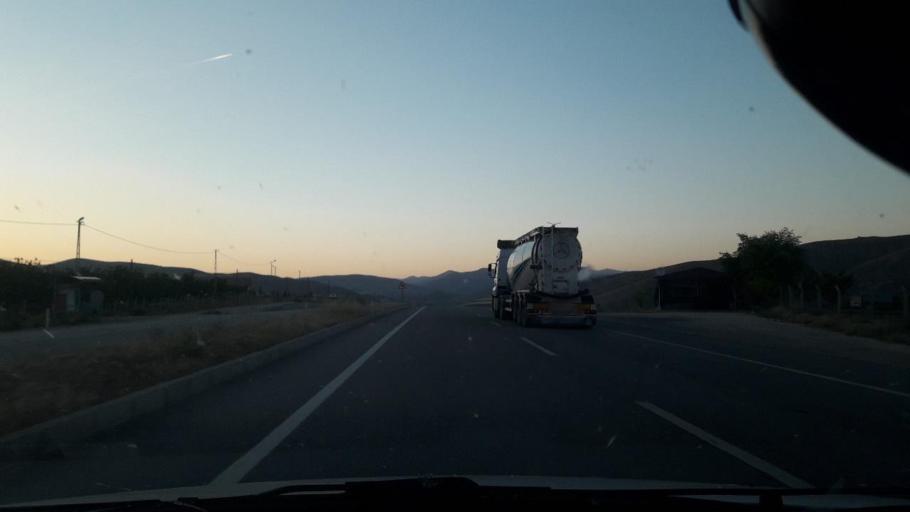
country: TR
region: Malatya
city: Yazihan
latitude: 38.6146
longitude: 38.1725
